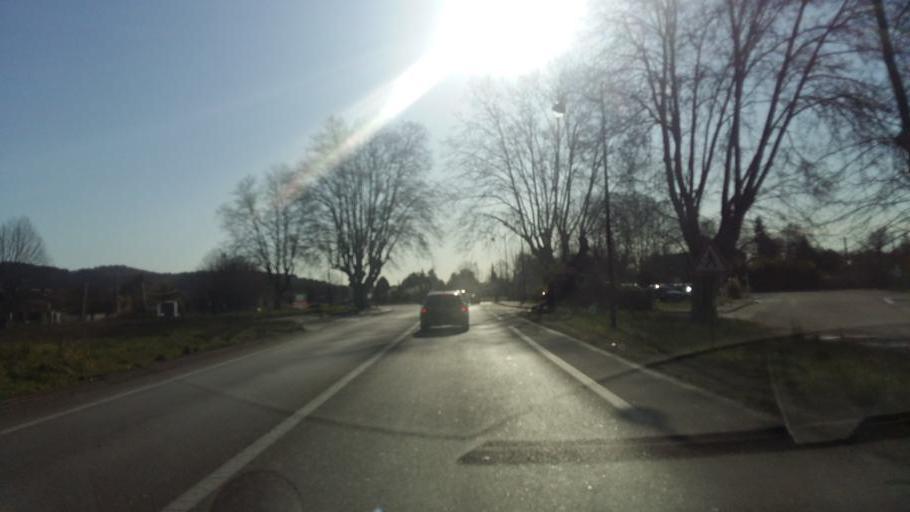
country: FR
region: Provence-Alpes-Cote d'Azur
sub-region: Departement du Vaucluse
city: Cadenet
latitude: 43.7261
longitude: 5.3755
